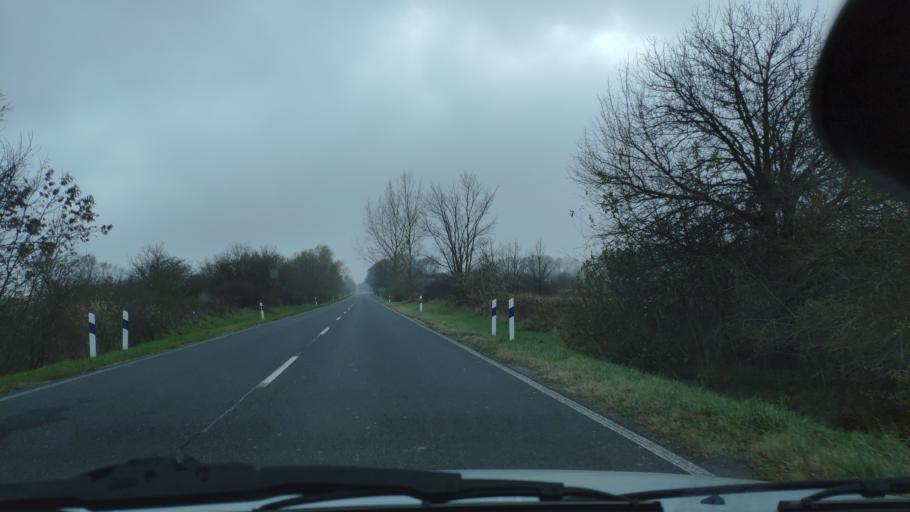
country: HU
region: Somogy
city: Balatonbereny
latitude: 46.6081
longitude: 17.2718
